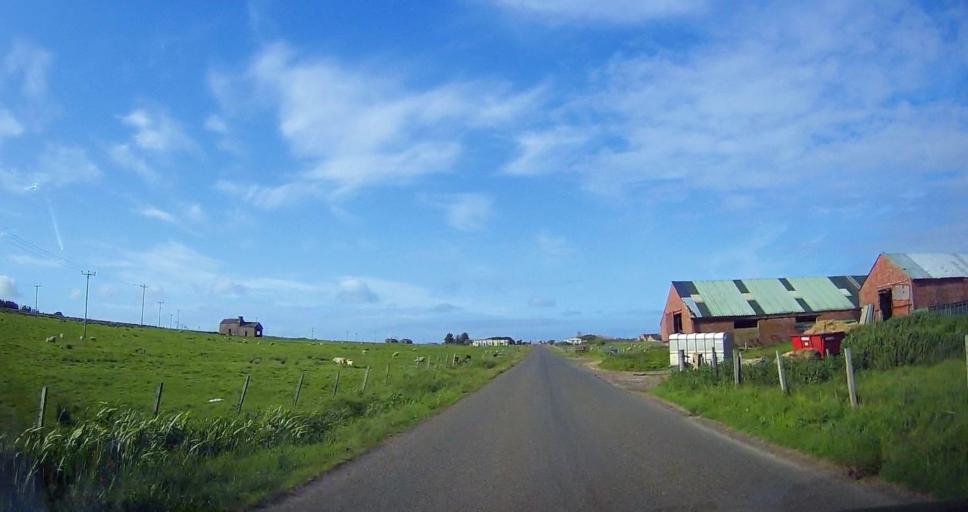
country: GB
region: Scotland
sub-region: Orkney Islands
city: Stromness
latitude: 58.8273
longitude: -3.2085
